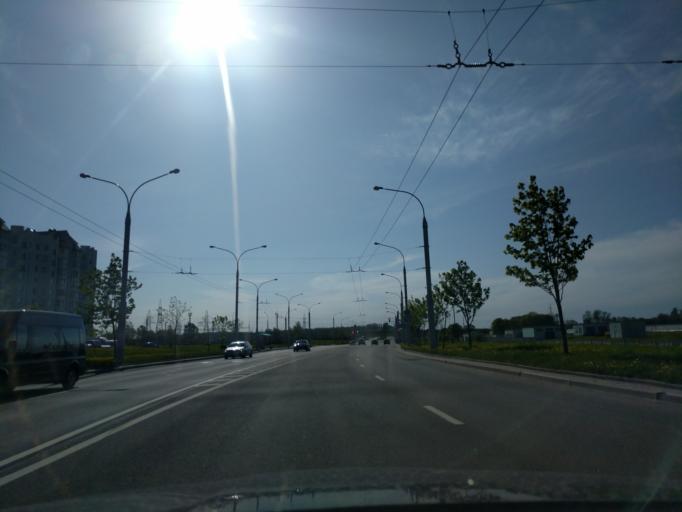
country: BY
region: Minsk
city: Novoye Medvezhino
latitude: 53.8955
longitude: 27.4185
